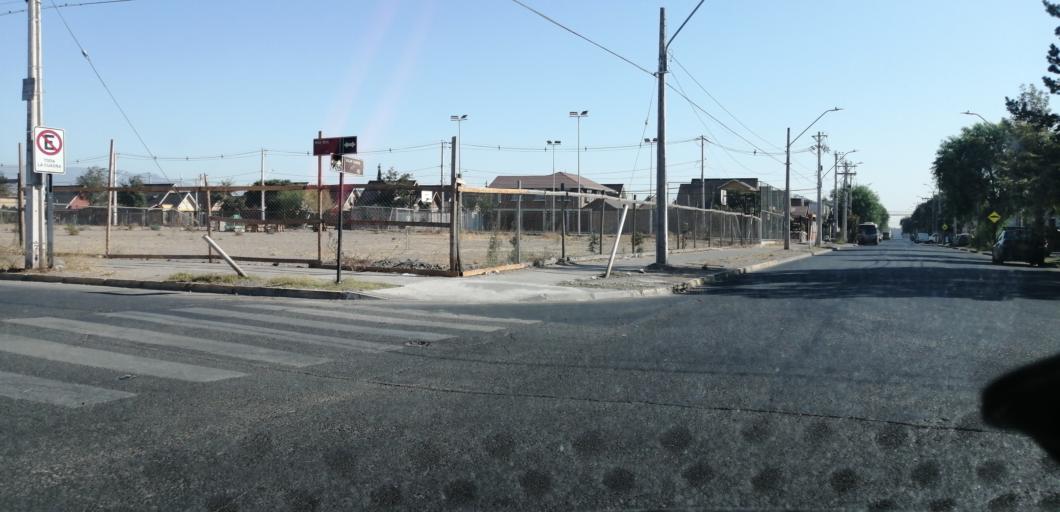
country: CL
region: Santiago Metropolitan
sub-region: Provincia de Santiago
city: Lo Prado
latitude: -33.4359
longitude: -70.7750
